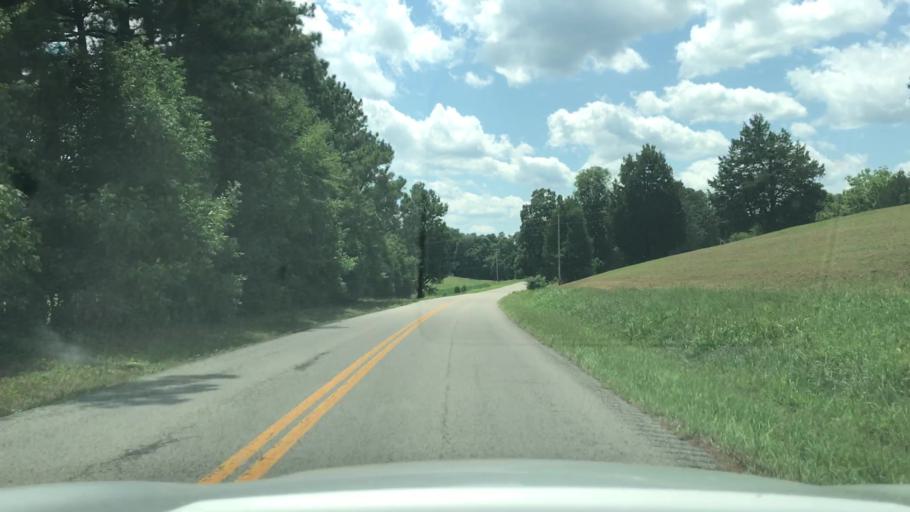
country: US
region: Kentucky
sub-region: Muhlenberg County
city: Greenville
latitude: 37.1389
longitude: -87.2649
